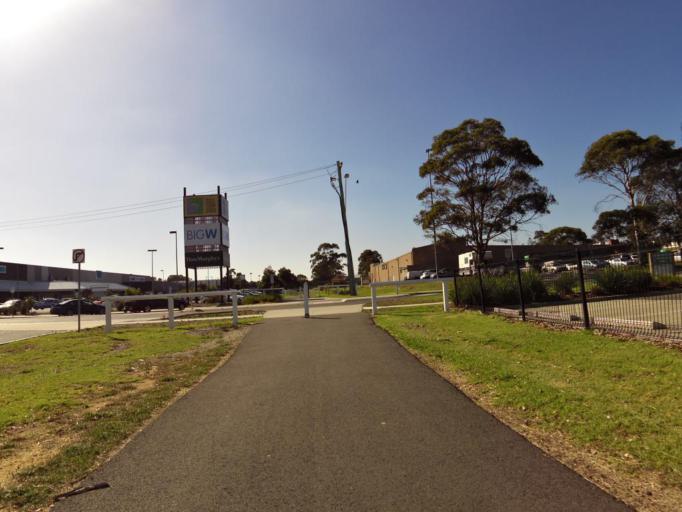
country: AU
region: Victoria
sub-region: Bass Coast
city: North Wonthaggi
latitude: -38.6043
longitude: 145.5879
